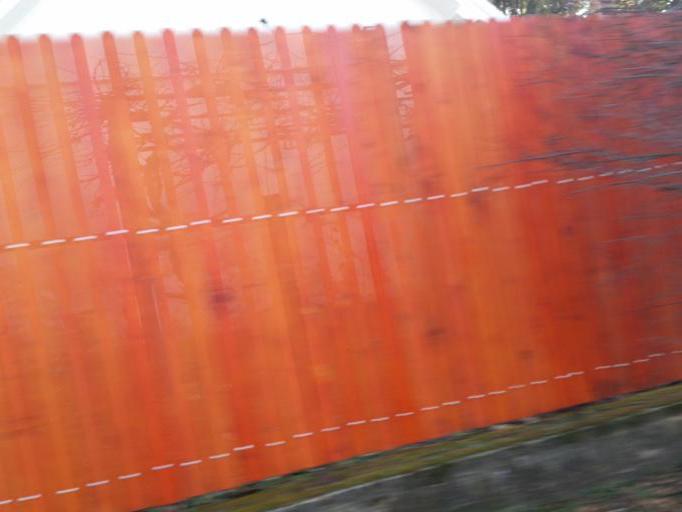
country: SK
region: Trnavsky
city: Vrbove
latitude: 48.6565
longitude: 17.7185
